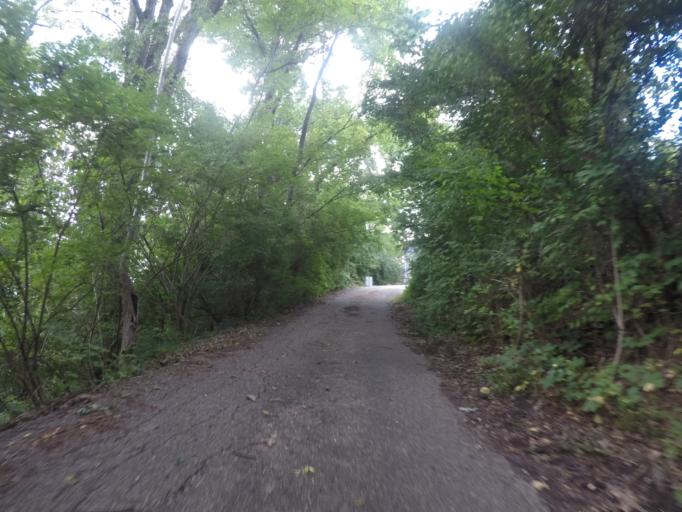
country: US
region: West Virginia
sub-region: Cabell County
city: Huntington
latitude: 38.4232
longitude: -82.3829
